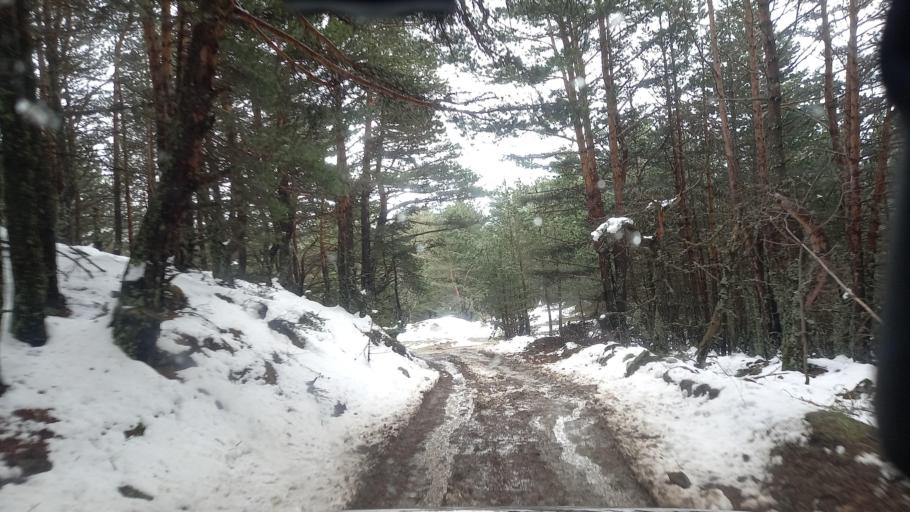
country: RU
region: North Ossetia
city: Mizur
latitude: 42.8092
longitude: 43.9600
